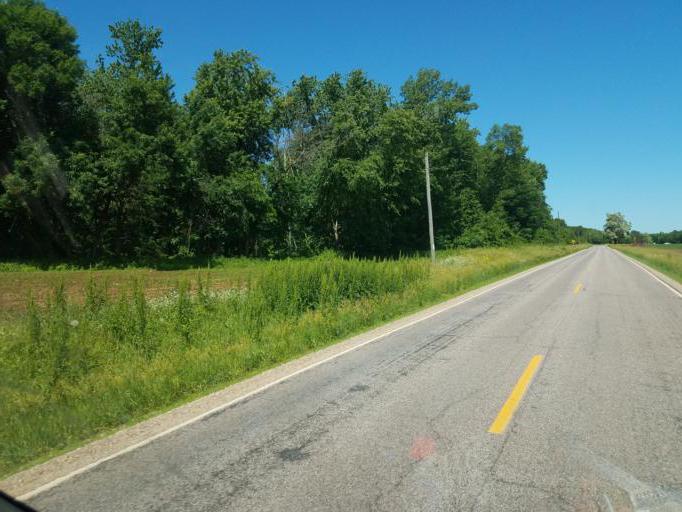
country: US
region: Wisconsin
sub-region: Adams County
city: Adams
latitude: 43.8278
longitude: -89.9115
